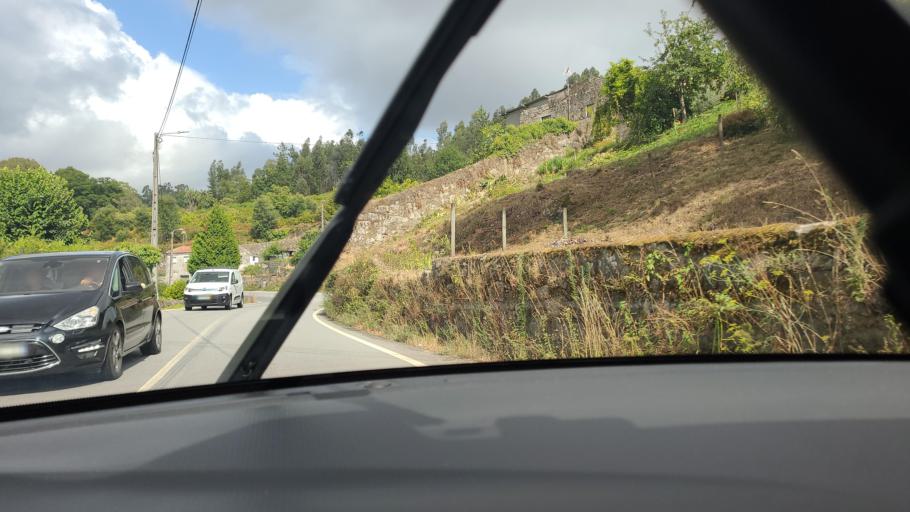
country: PT
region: Braga
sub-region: Braga
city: Adaufe
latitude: 41.5771
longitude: -8.4109
